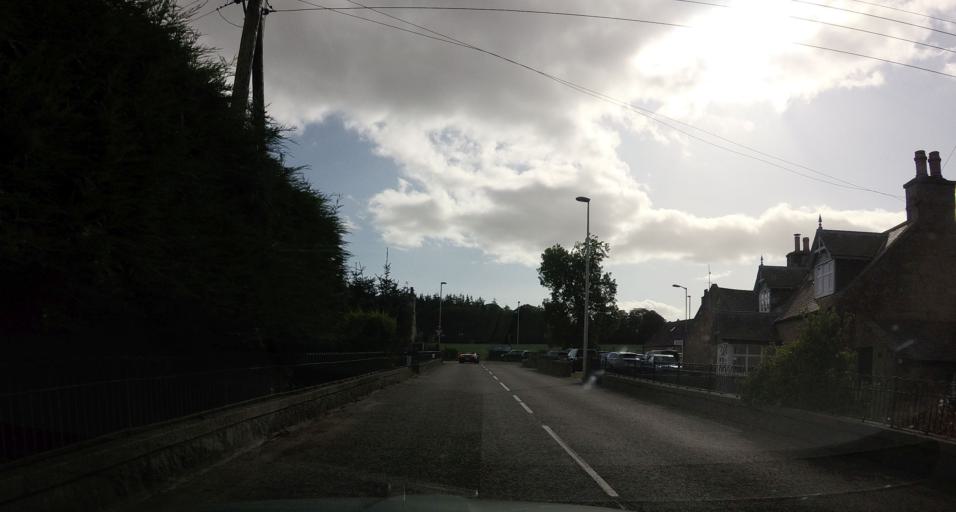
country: GB
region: Scotland
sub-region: Aberdeenshire
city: Kemnay
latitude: 57.1723
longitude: -2.4094
